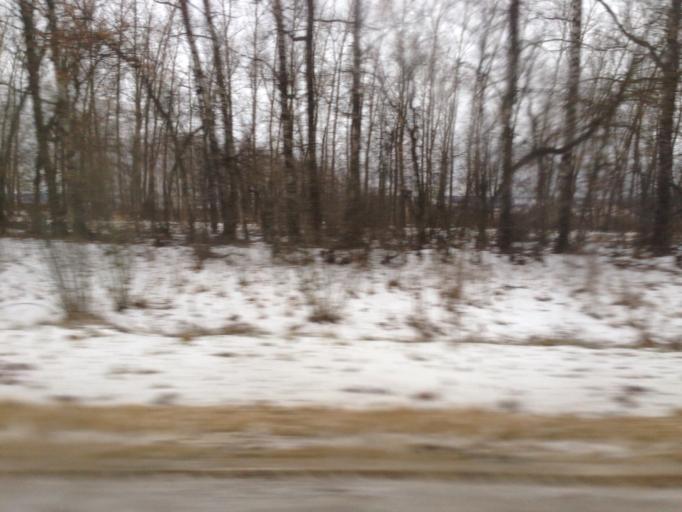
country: RU
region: Tula
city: Bolokhovo
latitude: 54.0909
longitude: 37.7723
